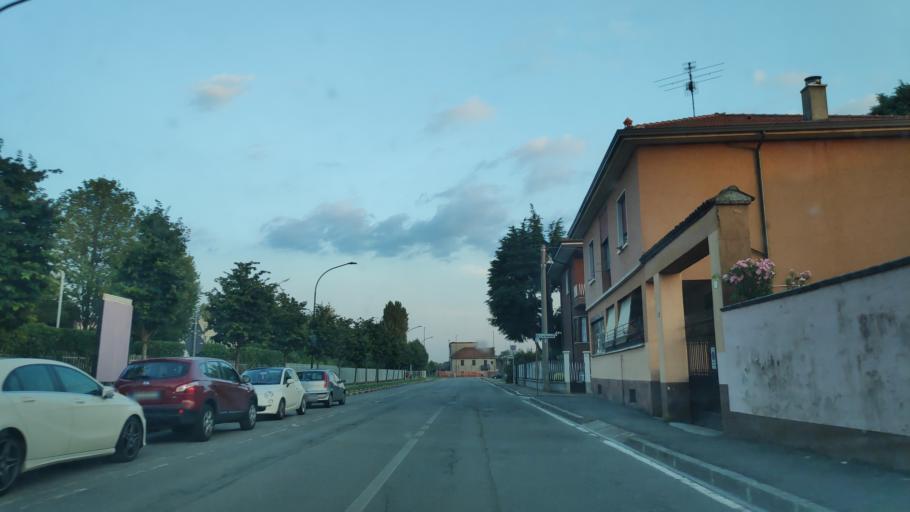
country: IT
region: Lombardy
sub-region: Citta metropolitana di Milano
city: Melzo
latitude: 45.4947
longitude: 9.4259
